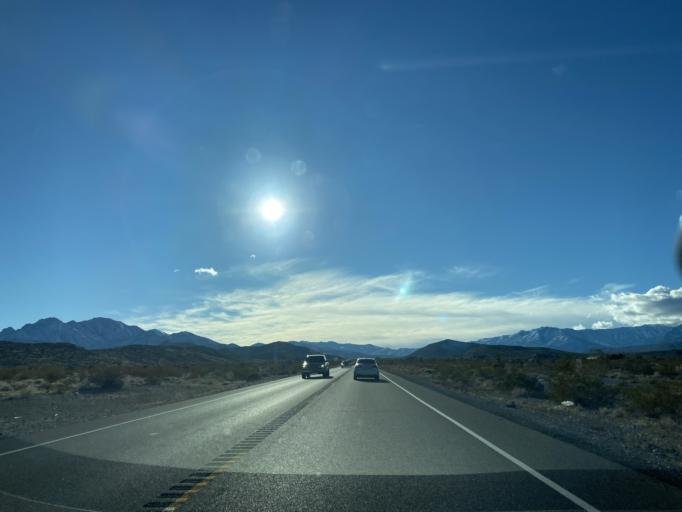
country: US
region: Nevada
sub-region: Clark County
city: Summerlin South
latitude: 36.3029
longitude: -115.4096
